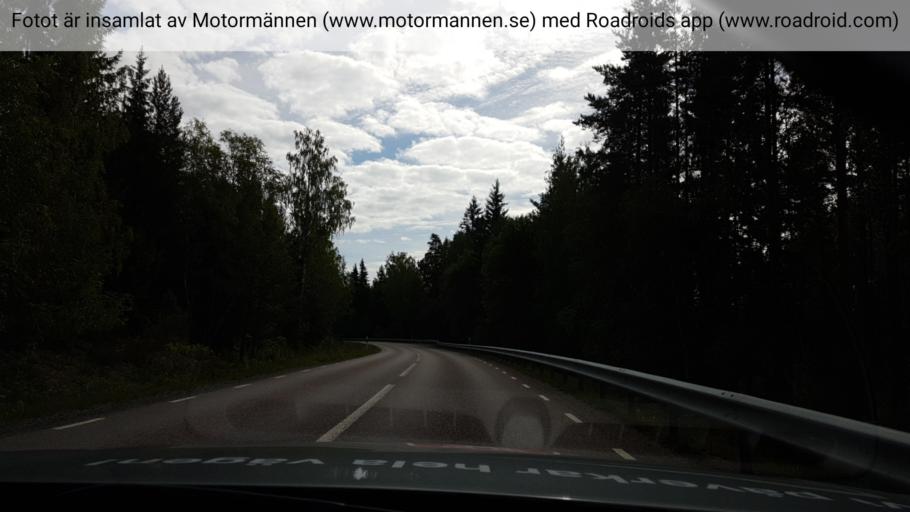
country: SE
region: Uppsala
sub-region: Heby Kommun
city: OEstervala
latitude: 60.0349
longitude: 17.2568
